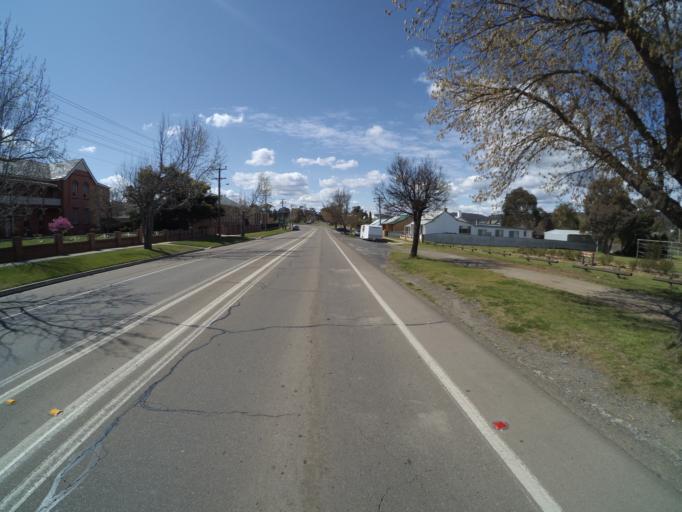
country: AU
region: New South Wales
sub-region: Goulburn Mulwaree
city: Goulburn
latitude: -34.7478
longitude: 149.7321
